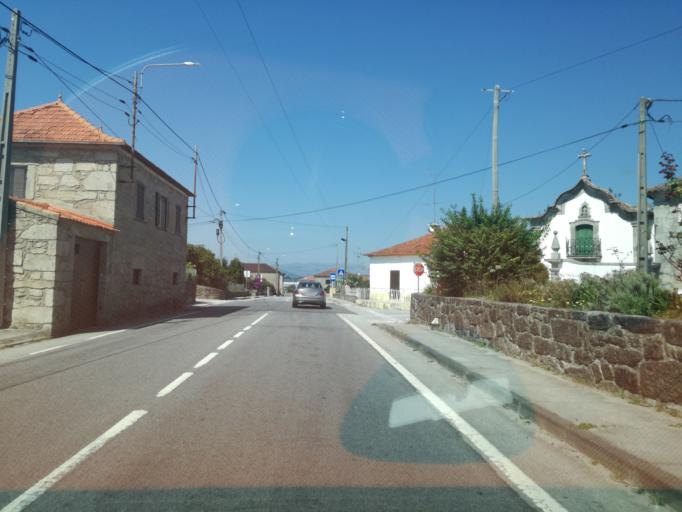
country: PT
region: Viana do Castelo
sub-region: Viana do Castelo
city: Darque
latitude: 41.6236
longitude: -8.7736
